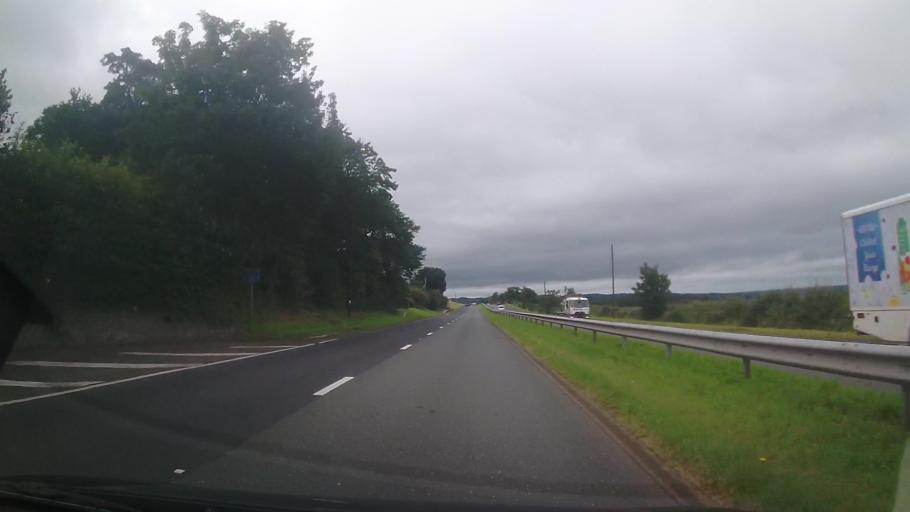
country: GB
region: Wales
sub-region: Gwynedd
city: Aber
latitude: 53.2319
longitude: -4.0285
